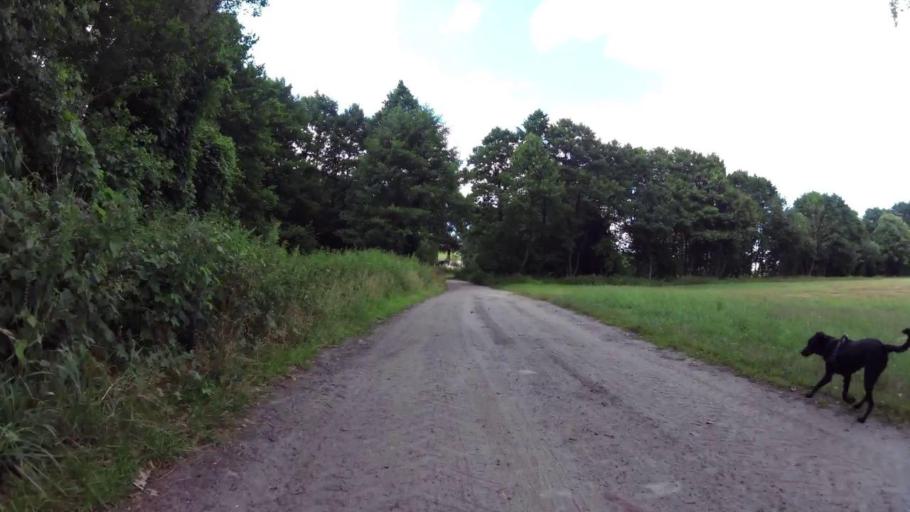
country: PL
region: West Pomeranian Voivodeship
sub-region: Powiat swidwinski
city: Swidwin
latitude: 53.6812
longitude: 15.7436
